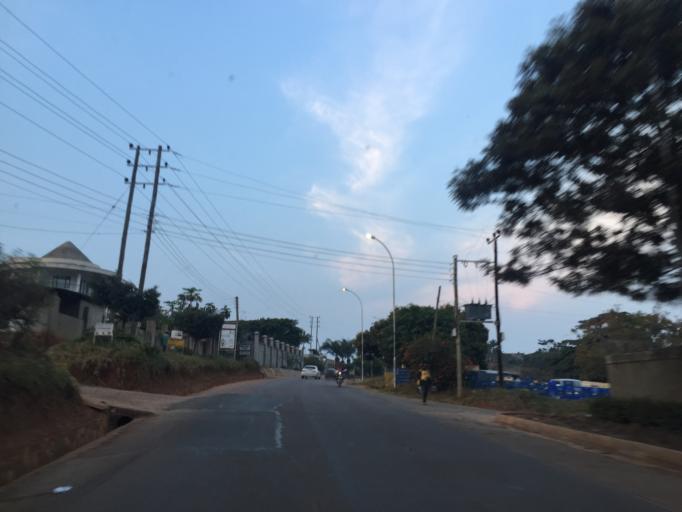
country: UG
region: Central Region
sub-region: Kampala District
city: Kampala
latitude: 0.2412
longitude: 32.6259
